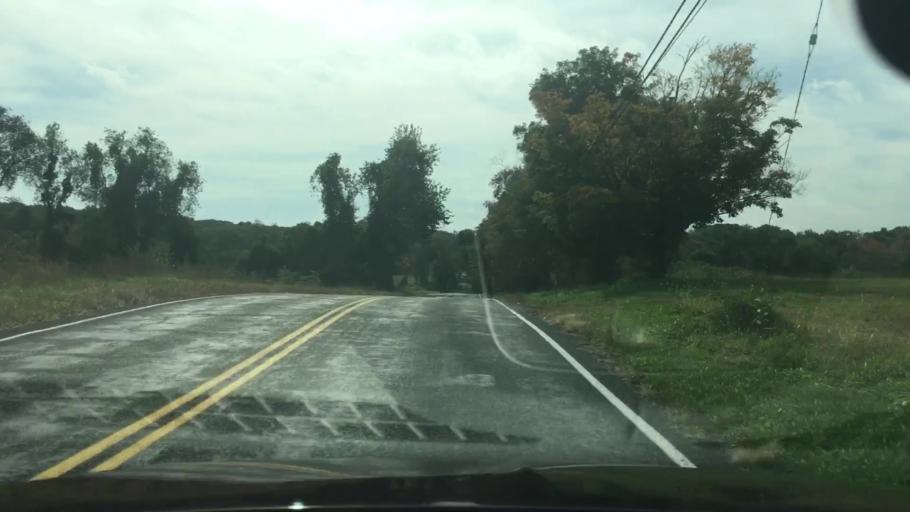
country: US
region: Connecticut
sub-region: Tolland County
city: Somers
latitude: 41.9580
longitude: -72.4827
